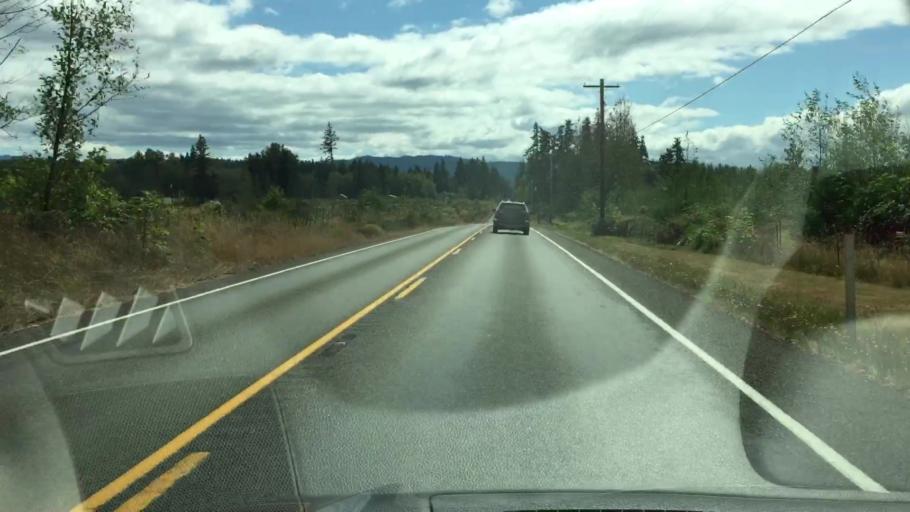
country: US
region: Washington
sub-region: Pierce County
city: Eatonville
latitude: 46.9061
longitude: -122.2979
